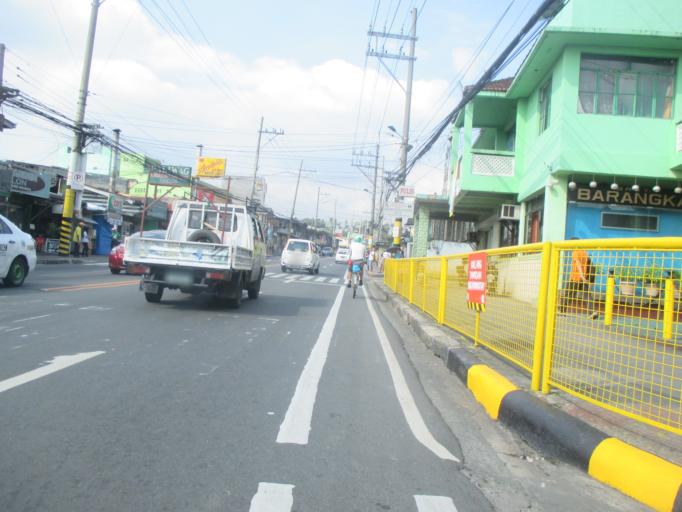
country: PH
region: Metro Manila
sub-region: Marikina
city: Calumpang
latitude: 14.6327
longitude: 121.0826
